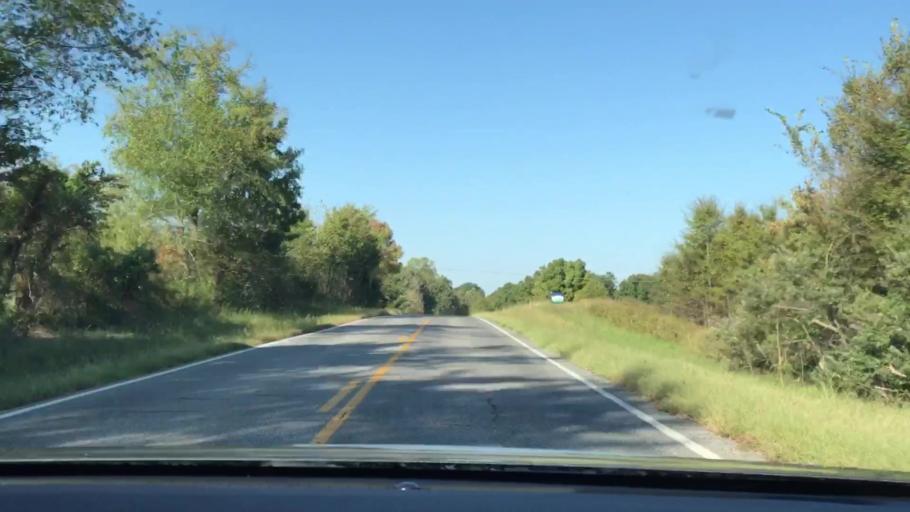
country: US
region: Kentucky
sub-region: Marshall County
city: Benton
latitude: 36.7639
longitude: -88.2044
